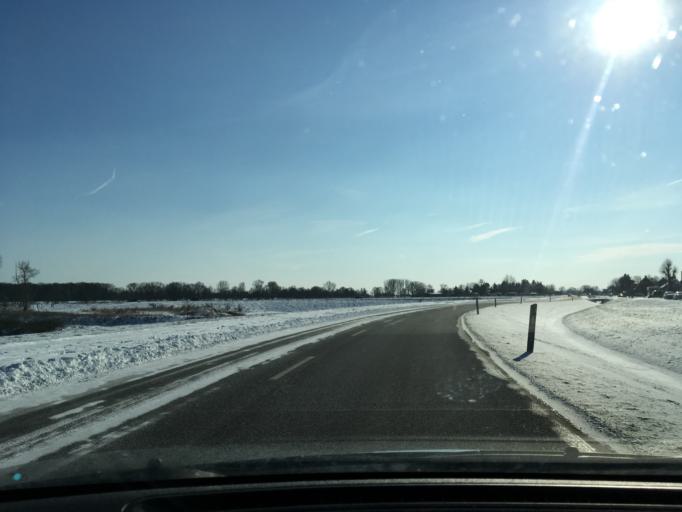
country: DE
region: Schleswig-Holstein
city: Escheburg
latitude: 53.4372
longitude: 10.3027
